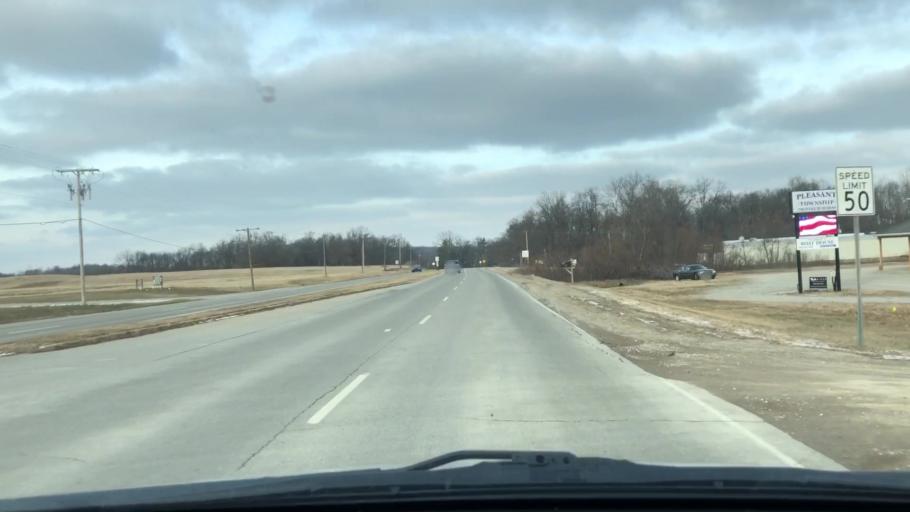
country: US
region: Indiana
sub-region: Steuben County
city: Angola
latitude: 41.6789
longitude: -85.0287
